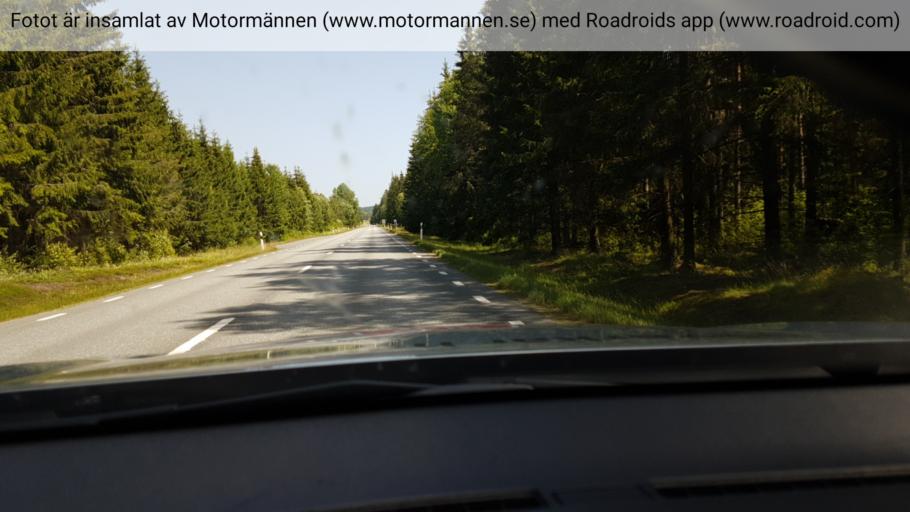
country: SE
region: Joenkoeping
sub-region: Nassjo Kommun
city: Bodafors
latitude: 57.4580
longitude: 14.7390
